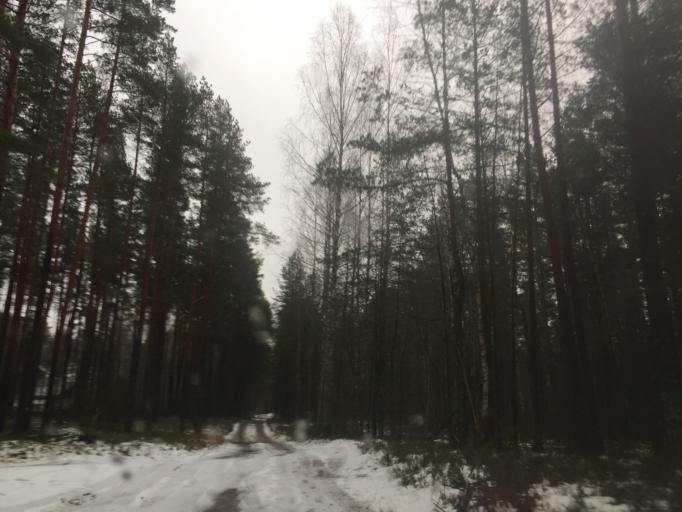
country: LV
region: Stopini
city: Ulbroka
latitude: 56.9484
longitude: 24.3422
